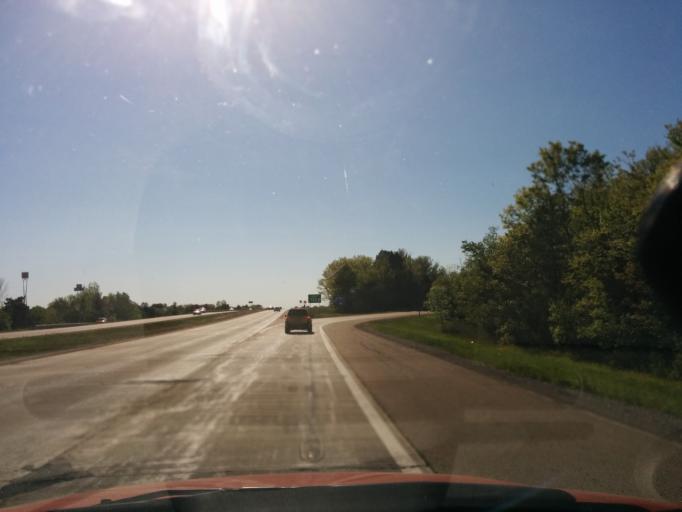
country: US
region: Michigan
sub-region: Midland County
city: Midland
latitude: 43.6561
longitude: -84.2420
